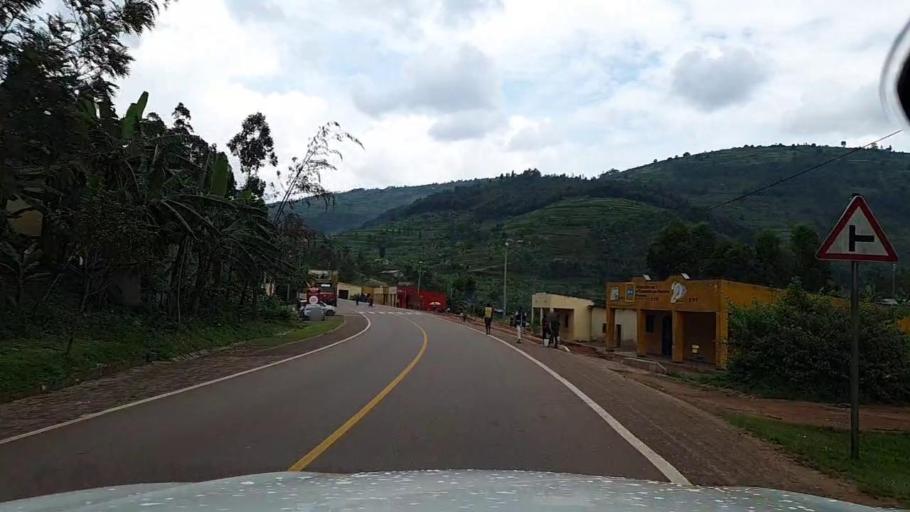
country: RW
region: Northern Province
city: Byumba
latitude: -1.7131
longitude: 30.1239
